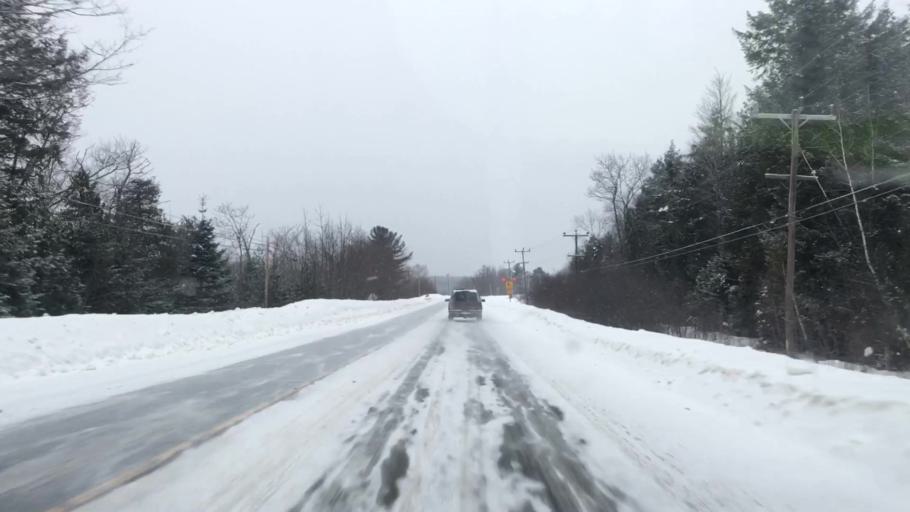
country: US
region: Maine
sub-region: Penobscot County
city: Medway
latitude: 45.5952
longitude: -68.4867
